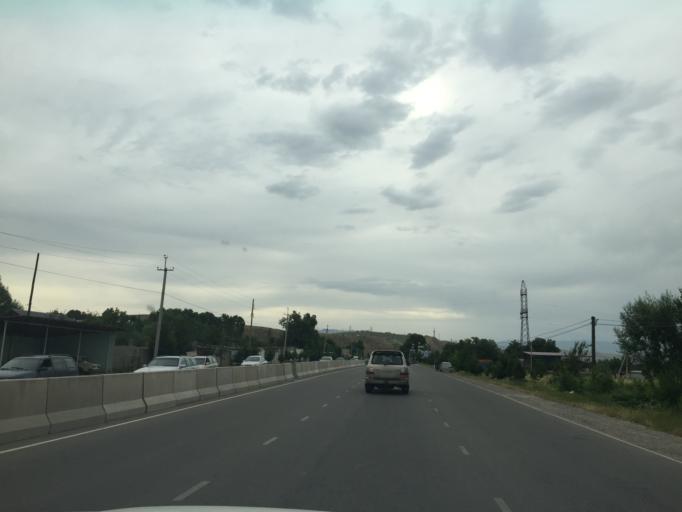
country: TJ
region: Republican Subordination
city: Vahdat
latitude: 38.5564
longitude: 68.9483
